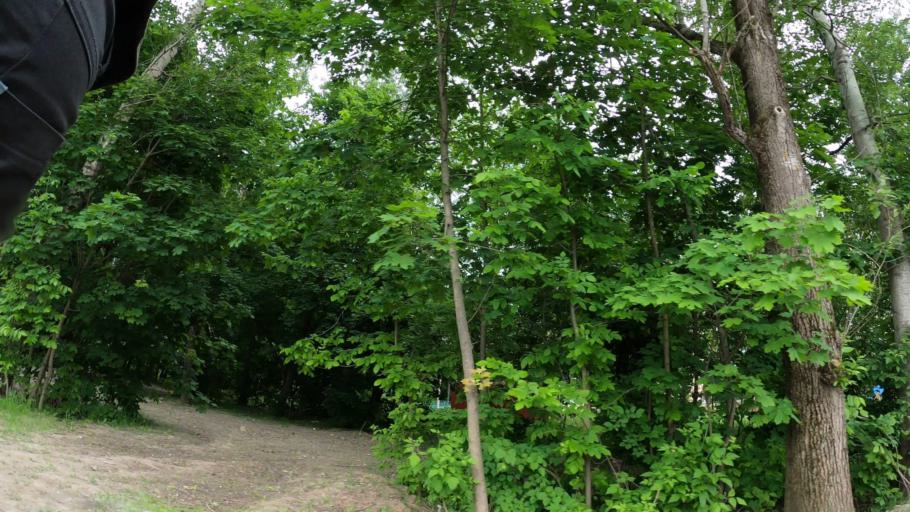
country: RU
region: Moskovskaya
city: Yubileyny
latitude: 55.9403
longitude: 37.8375
